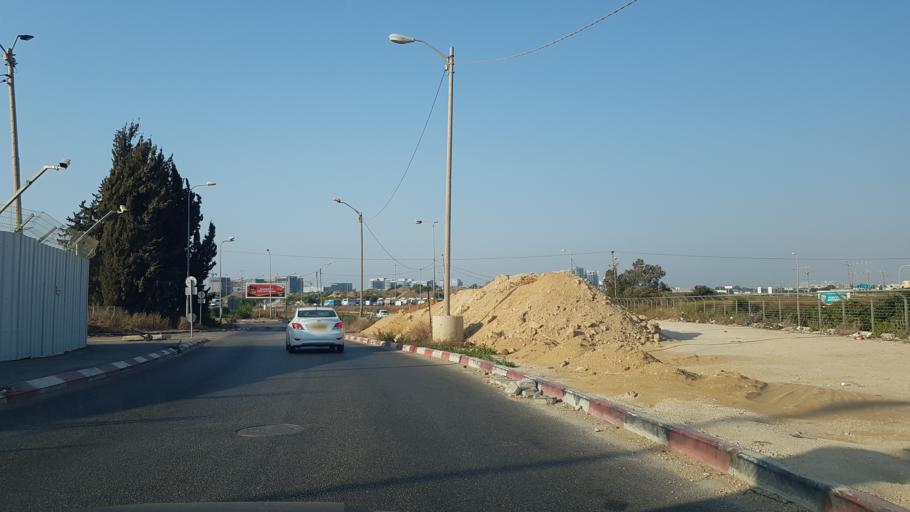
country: IL
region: Tel Aviv
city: Herzliyya
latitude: 32.1450
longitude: 34.8070
